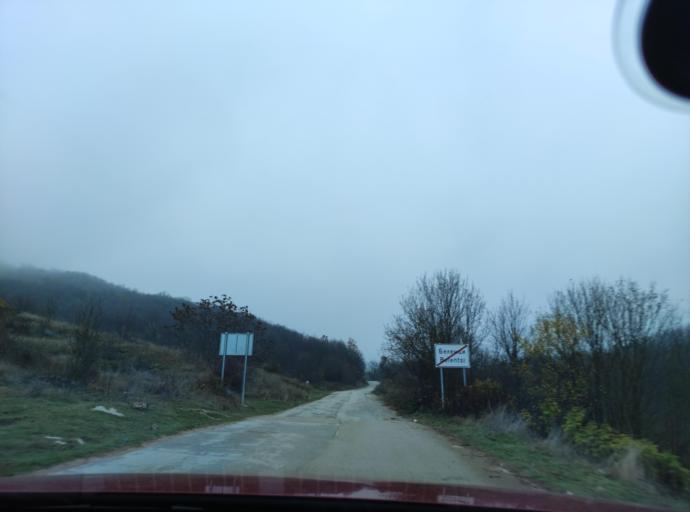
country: BG
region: Lovech
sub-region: Obshtina Yablanitsa
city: Yablanitsa
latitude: 43.1148
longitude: 24.0658
